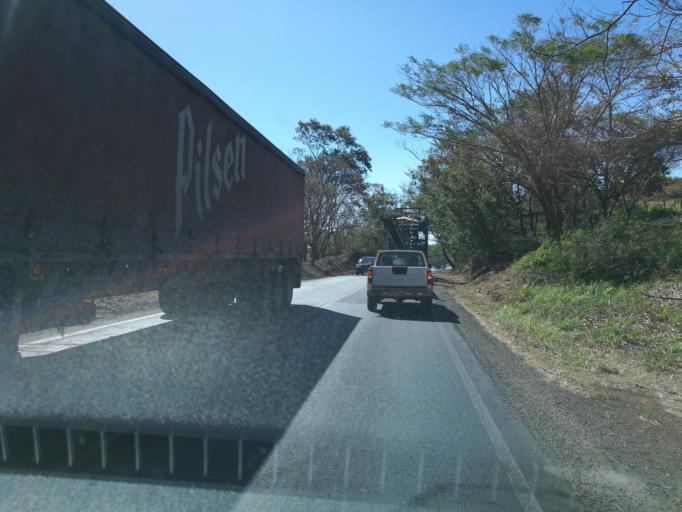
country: CR
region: Puntarenas
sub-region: Canton Central de Puntarenas
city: Puntarenas
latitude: 10.0956
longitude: -84.8567
